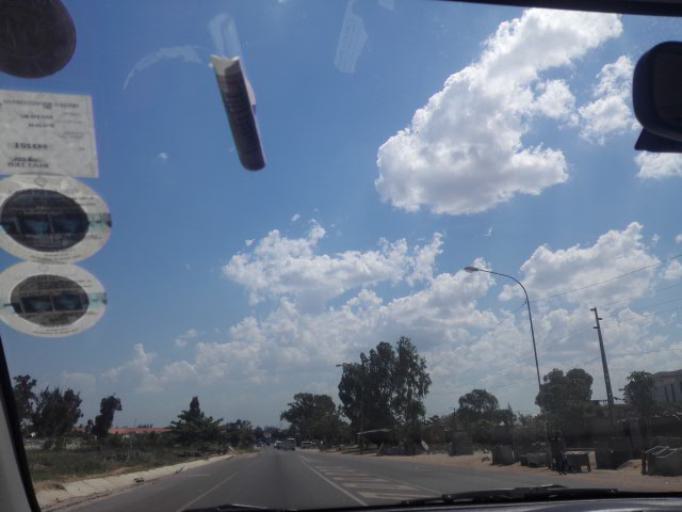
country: MZ
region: Maputo
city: Matola
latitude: -25.9683
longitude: 32.4432
